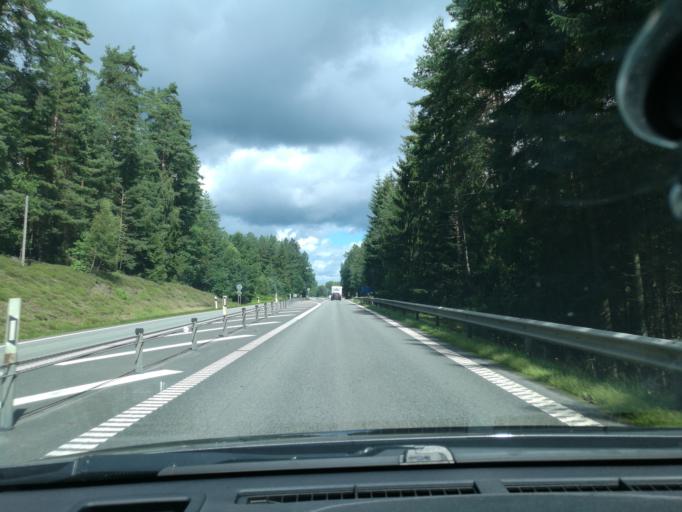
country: SE
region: Skane
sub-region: Osby Kommun
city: Osby
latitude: 56.3715
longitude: 14.0312
